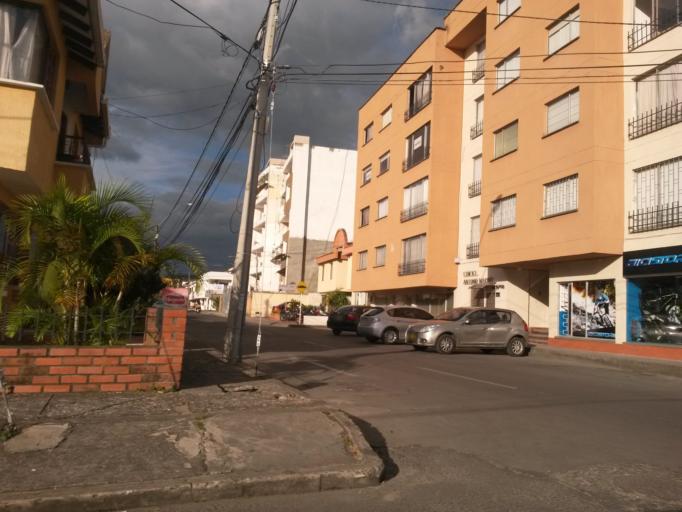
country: CO
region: Cauca
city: Popayan
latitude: 2.4557
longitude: -76.5994
